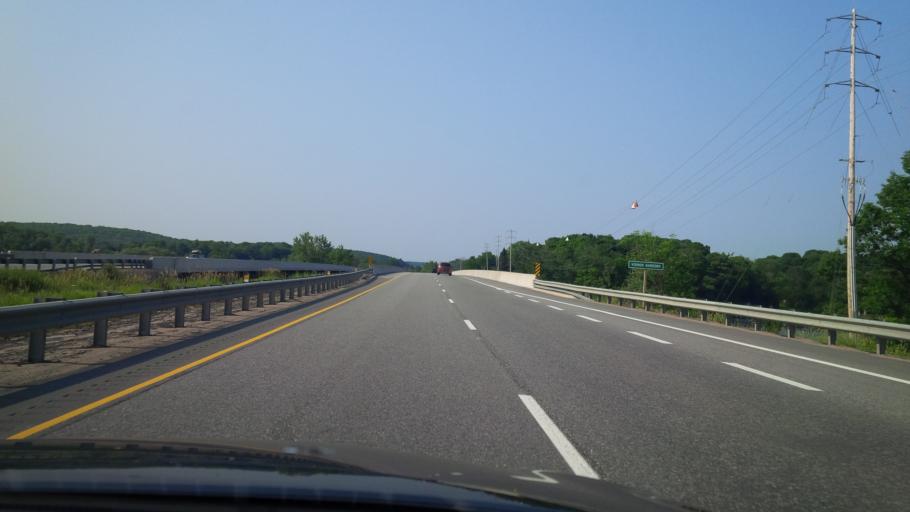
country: CA
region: Ontario
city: Huntsville
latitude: 45.3257
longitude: -79.2399
